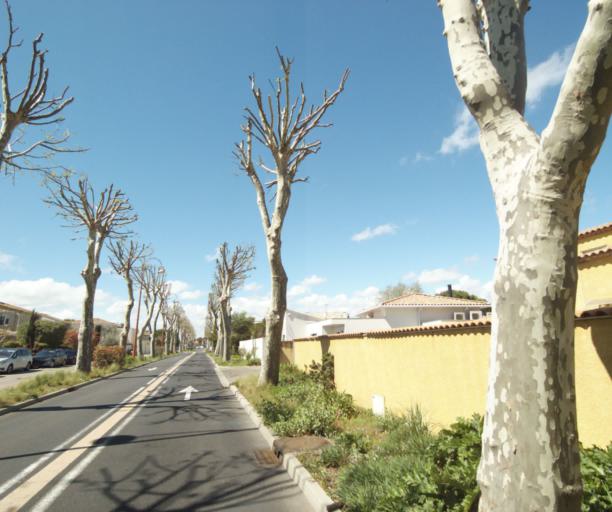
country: FR
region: Languedoc-Roussillon
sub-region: Departement de l'Herault
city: Perols
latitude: 43.5601
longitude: 3.9569
